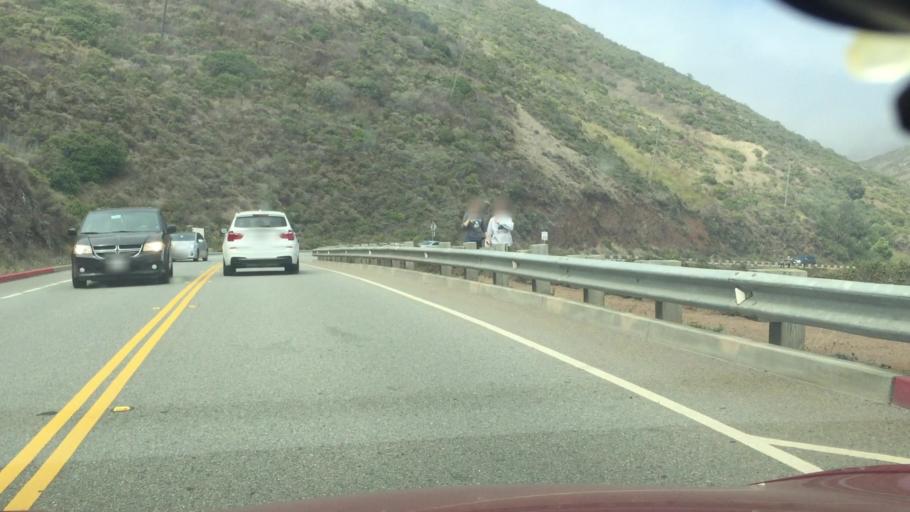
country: US
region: California
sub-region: Marin County
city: Sausalito
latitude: 37.8301
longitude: -122.4835
